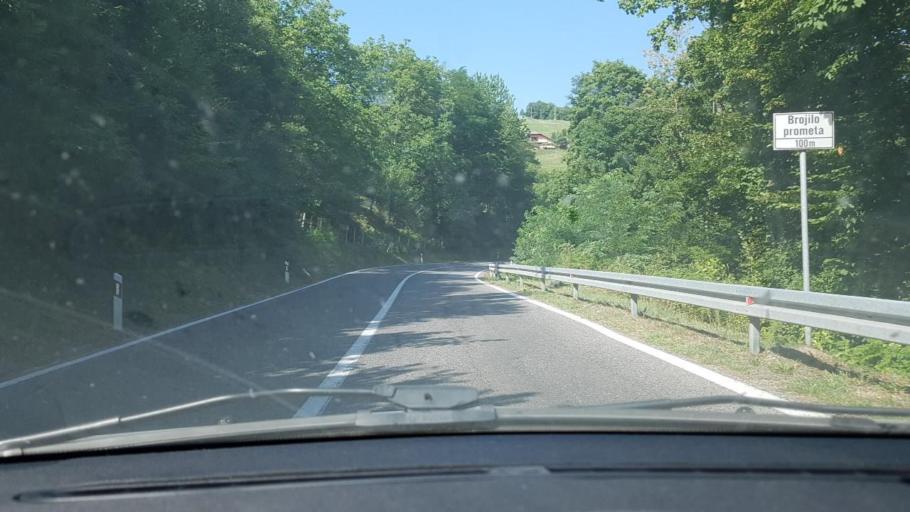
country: BA
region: Federation of Bosnia and Herzegovina
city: Skokovi
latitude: 45.0453
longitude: 15.9094
